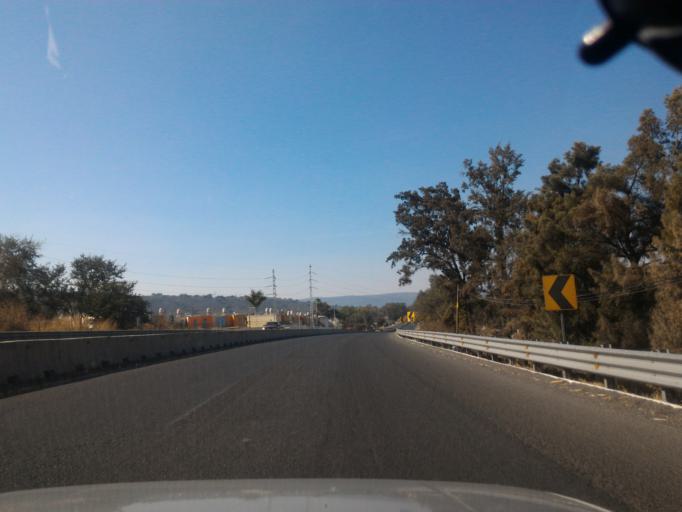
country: MX
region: Jalisco
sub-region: Poncitlan
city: Cuitzeo (La Estancia)
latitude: 20.3489
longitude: -102.7920
